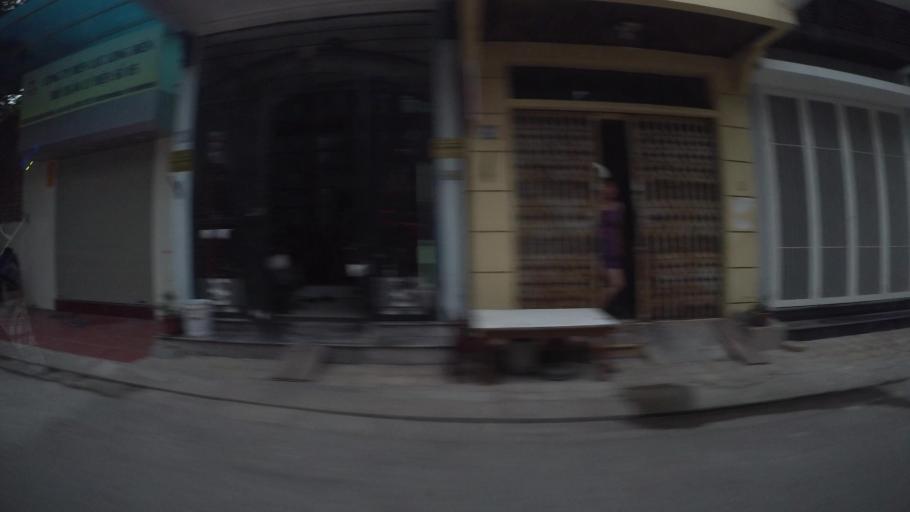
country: VN
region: Ha Noi
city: Trau Quy
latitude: 21.0369
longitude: 105.9036
